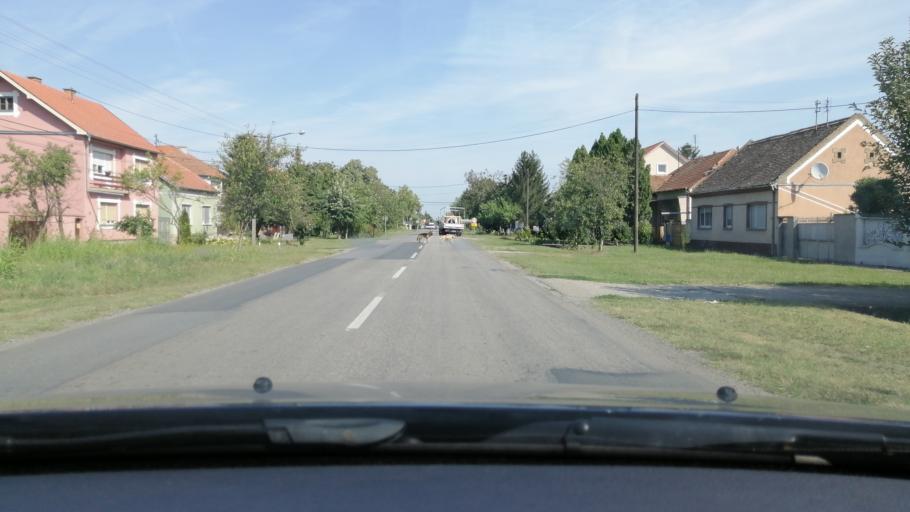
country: RS
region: Autonomna Pokrajina Vojvodina
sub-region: Juznobanatski Okrug
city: Kovacica
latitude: 45.1088
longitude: 20.6193
